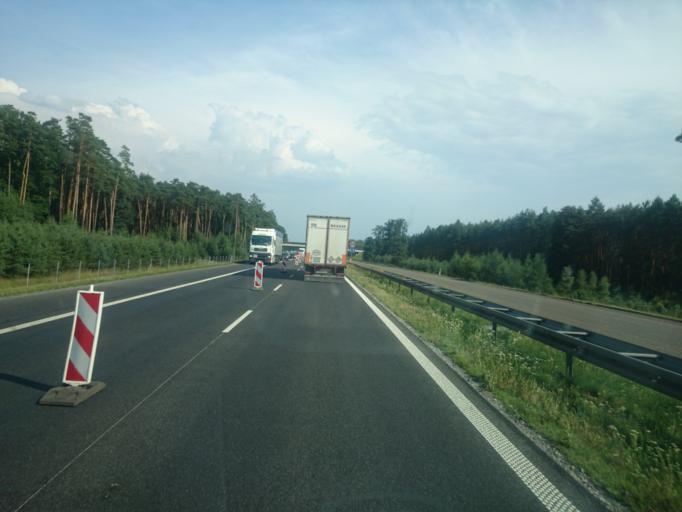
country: PL
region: Opole Voivodeship
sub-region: Powiat opolski
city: Komprachcice
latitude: 50.5958
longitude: 17.8008
